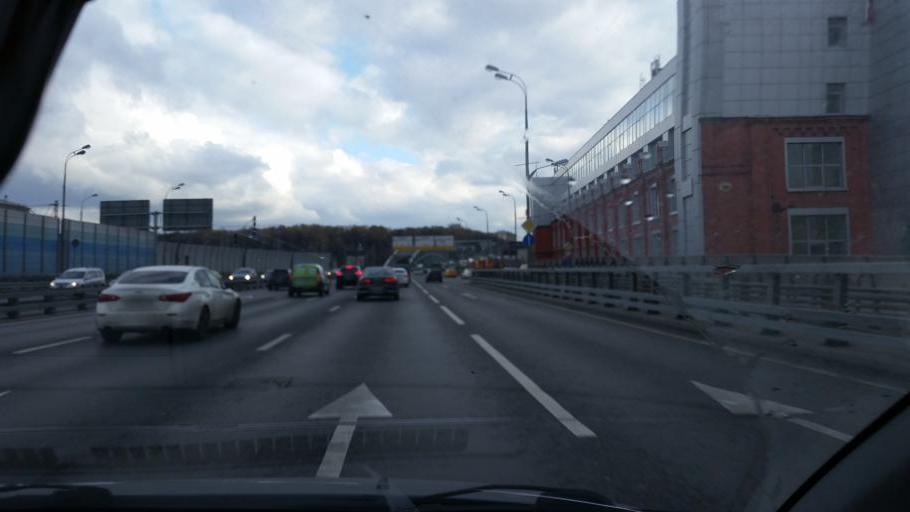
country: RU
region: Moskovskaya
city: Leninskiye Gory
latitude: 55.7162
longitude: 37.5728
